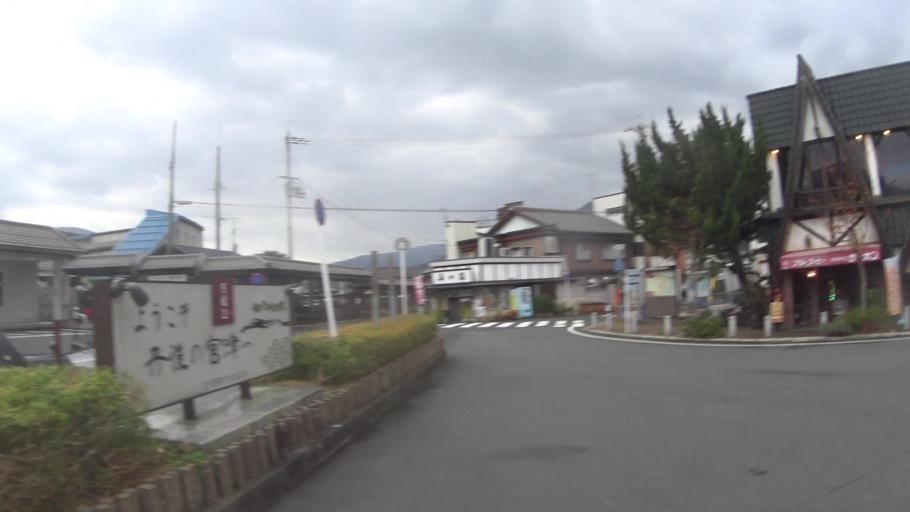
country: JP
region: Kyoto
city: Miyazu
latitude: 35.5346
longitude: 135.1995
